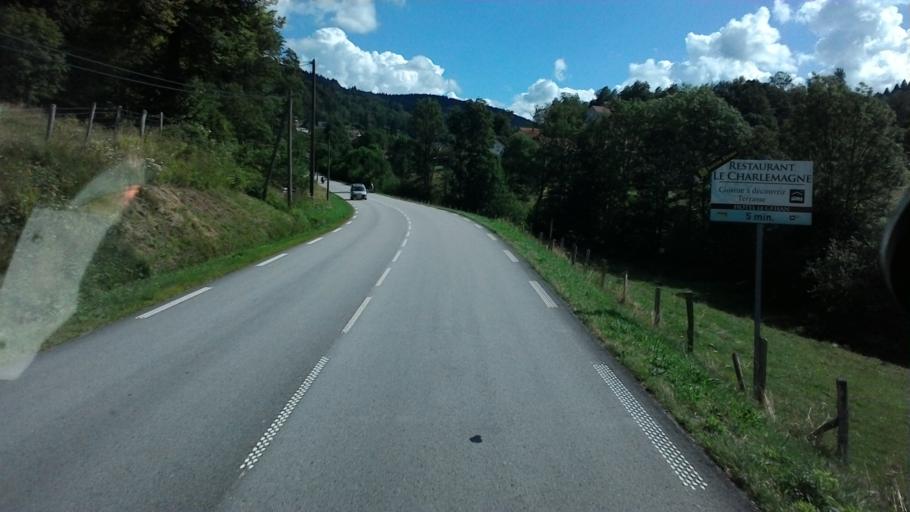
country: FR
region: Lorraine
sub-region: Departement des Vosges
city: Le Menil
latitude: 47.9139
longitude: 6.7892
